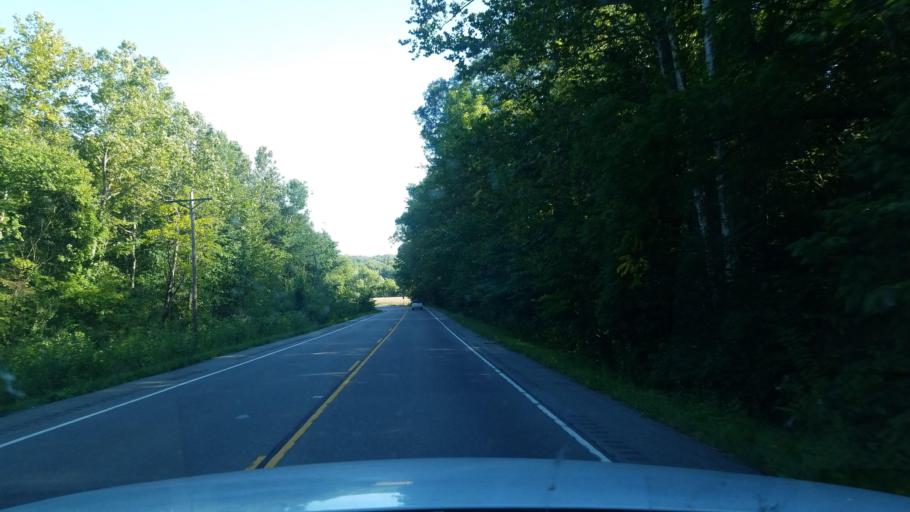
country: US
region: Illinois
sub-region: Saline County
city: Harrisburg
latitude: 37.5982
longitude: -88.4577
